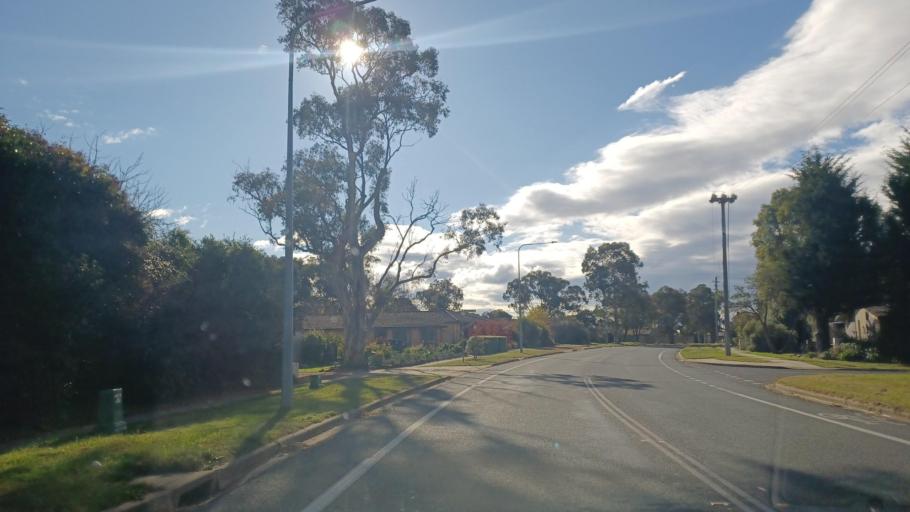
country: AU
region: Australian Capital Territory
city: Belconnen
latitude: -35.1962
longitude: 149.0417
